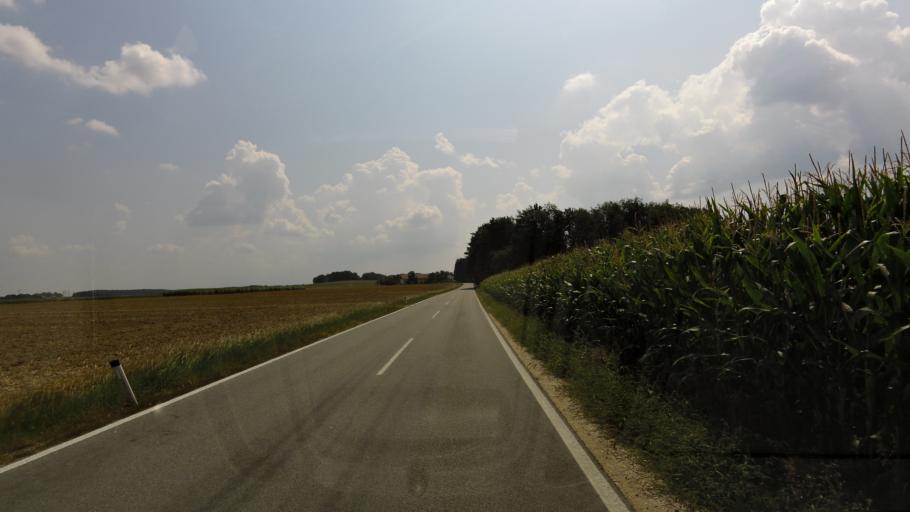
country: AT
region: Upper Austria
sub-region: Politischer Bezirk Ried im Innkreis
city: Waldzell
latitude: 48.1754
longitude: 13.4085
